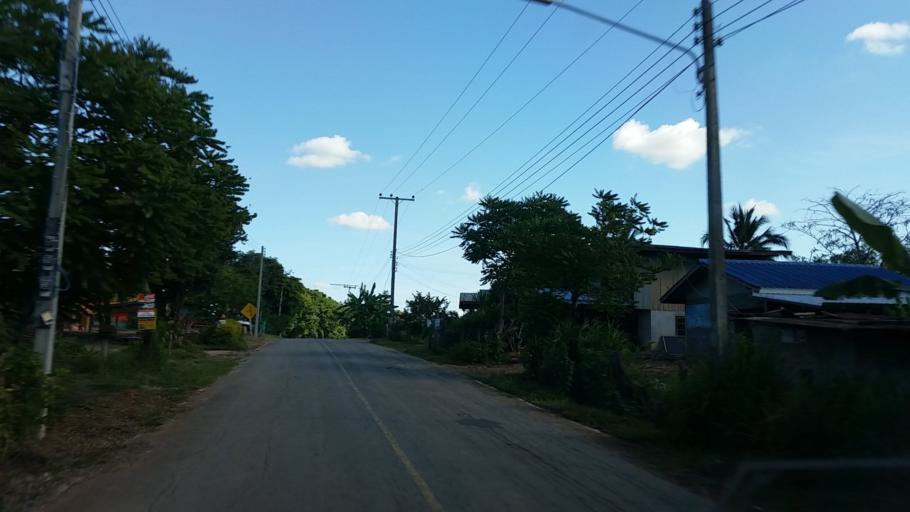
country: TH
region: Chaiyaphum
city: Thep Sathit
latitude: 15.5561
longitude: 101.4447
